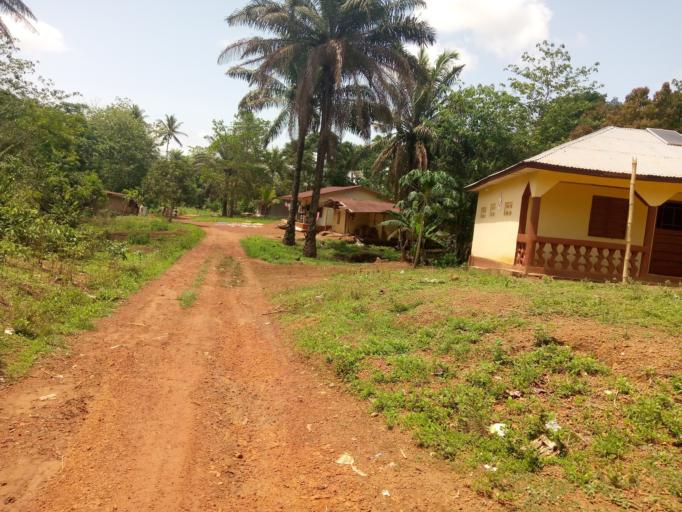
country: SL
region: Western Area
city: Waterloo
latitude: 8.3560
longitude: -12.9246
